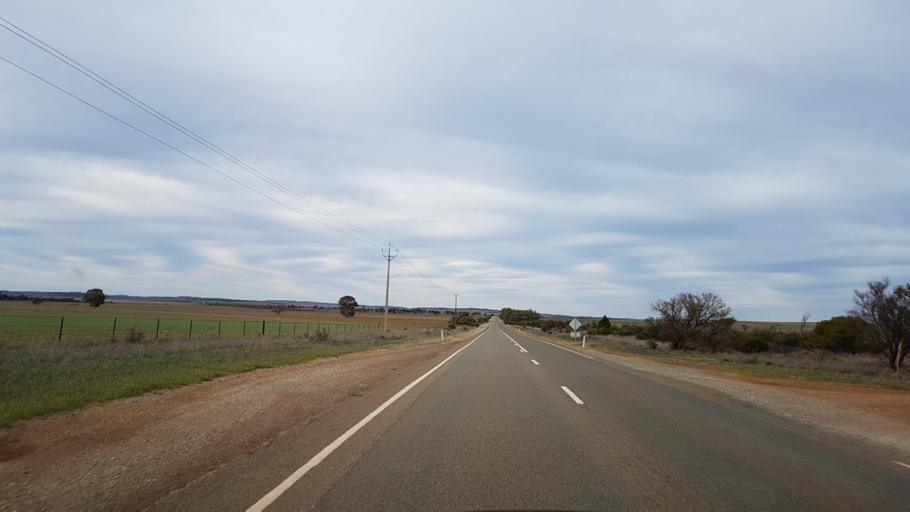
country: AU
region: South Australia
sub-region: Peterborough
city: Peterborough
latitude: -33.0010
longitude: 138.7773
